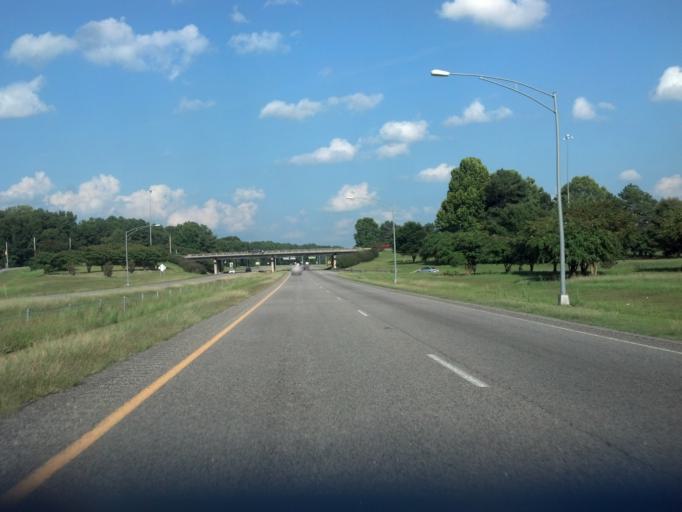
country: US
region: North Carolina
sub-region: Edgecombe County
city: Tarboro
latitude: 35.8860
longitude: -77.5505
